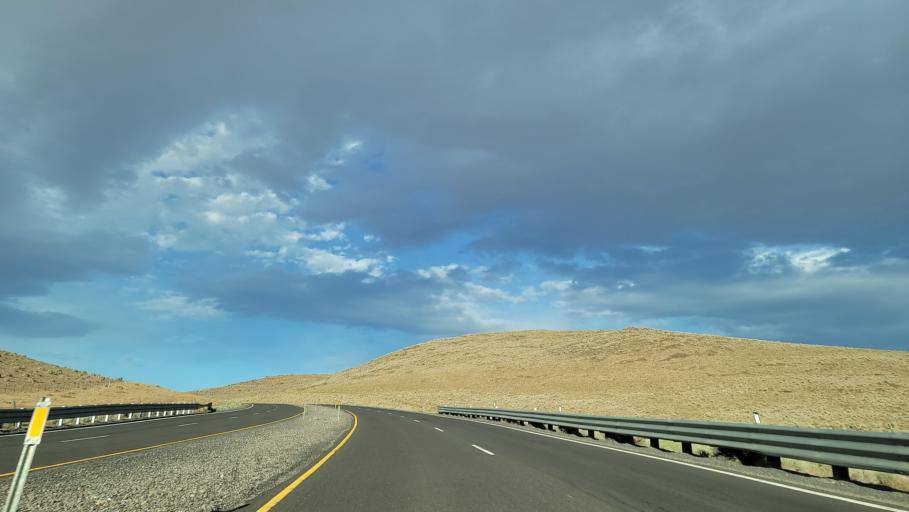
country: US
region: Nevada
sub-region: Lyon County
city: Stagecoach
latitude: 39.5091
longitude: -119.4603
